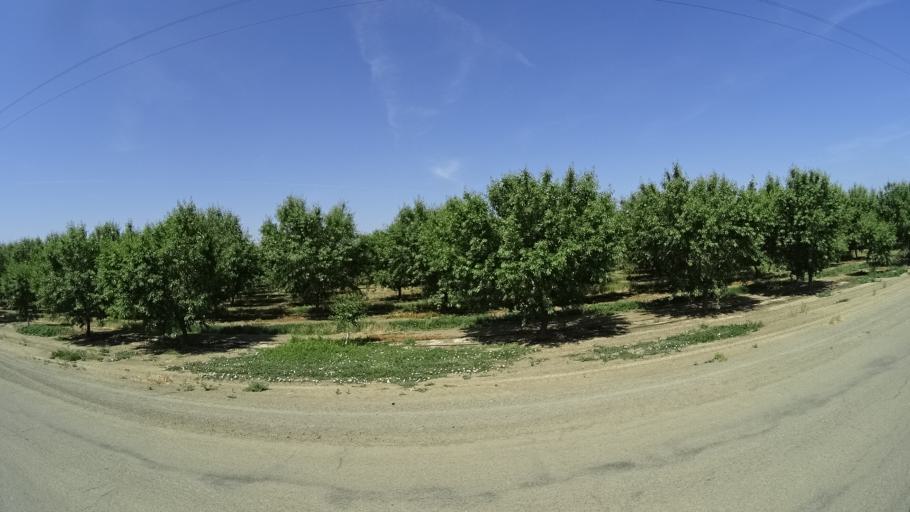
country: US
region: California
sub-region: Kings County
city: Kettleman City
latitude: 36.0824
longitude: -120.0037
